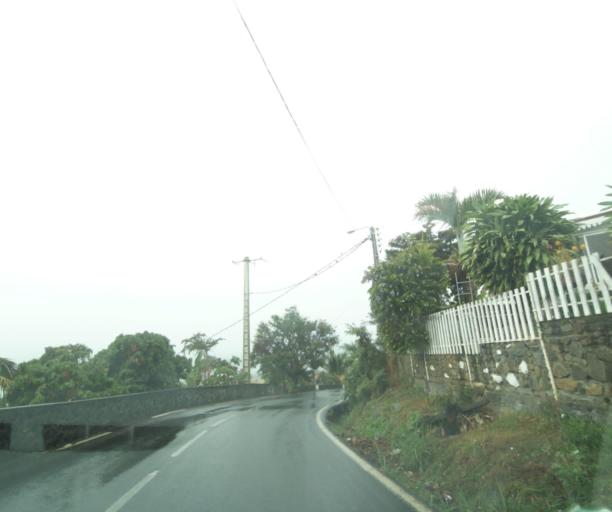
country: RE
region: Reunion
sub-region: Reunion
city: Saint-Paul
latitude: -21.0273
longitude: 55.2858
